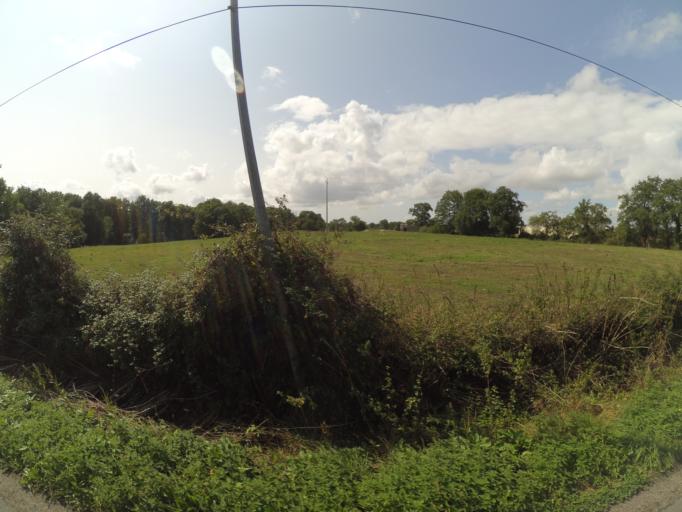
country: FR
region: Pays de la Loire
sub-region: Departement de la Vendee
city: La Bernardiere
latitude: 47.0338
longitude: -1.2368
